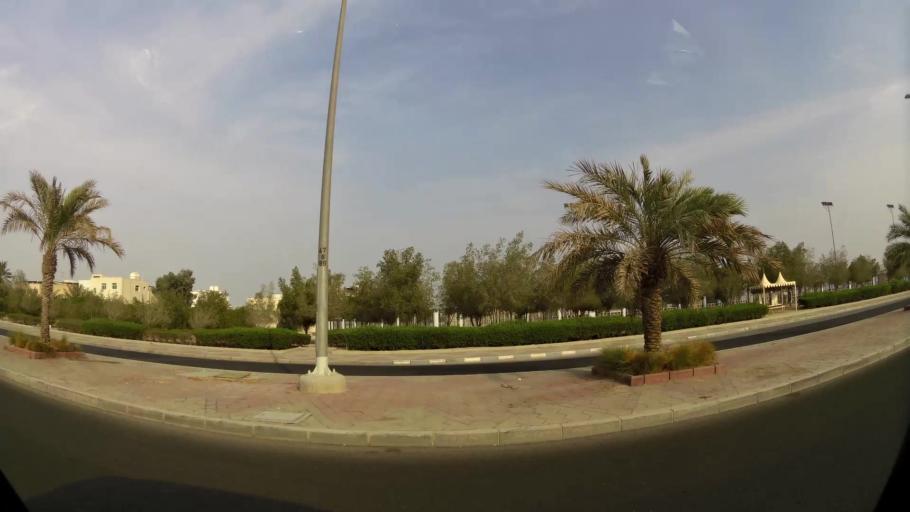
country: KW
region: Mubarak al Kabir
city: Sabah as Salim
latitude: 29.2558
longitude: 48.0544
